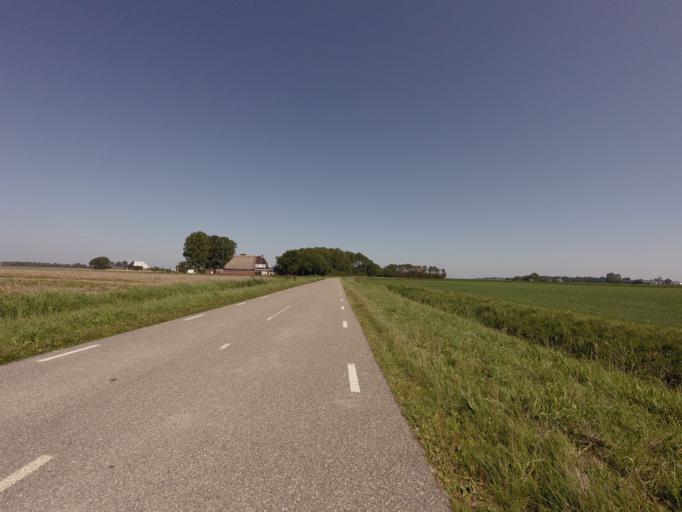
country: NL
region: Friesland
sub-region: Gemeente Dongeradeel
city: Ternaard
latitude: 53.3653
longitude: 5.9814
